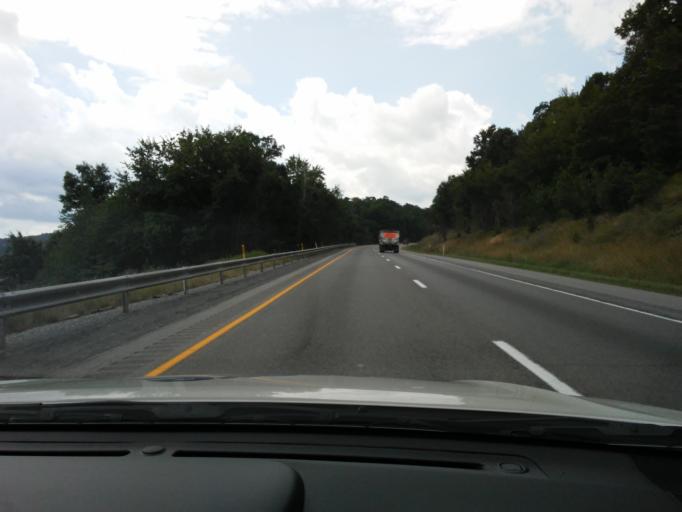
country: US
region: Pennsylvania
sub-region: Centre County
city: Stormstown
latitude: 40.9801
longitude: -78.0391
